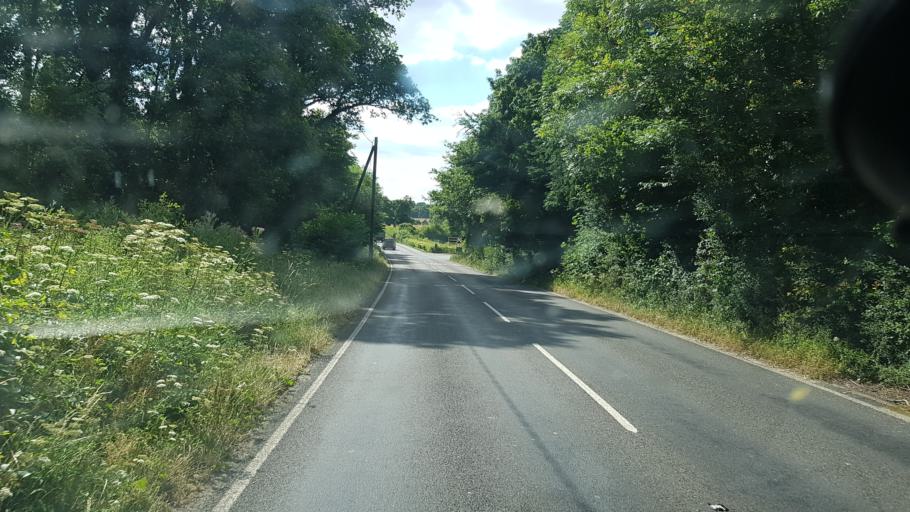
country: GB
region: England
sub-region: West Sussex
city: Southwater
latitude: 50.9928
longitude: -0.3448
